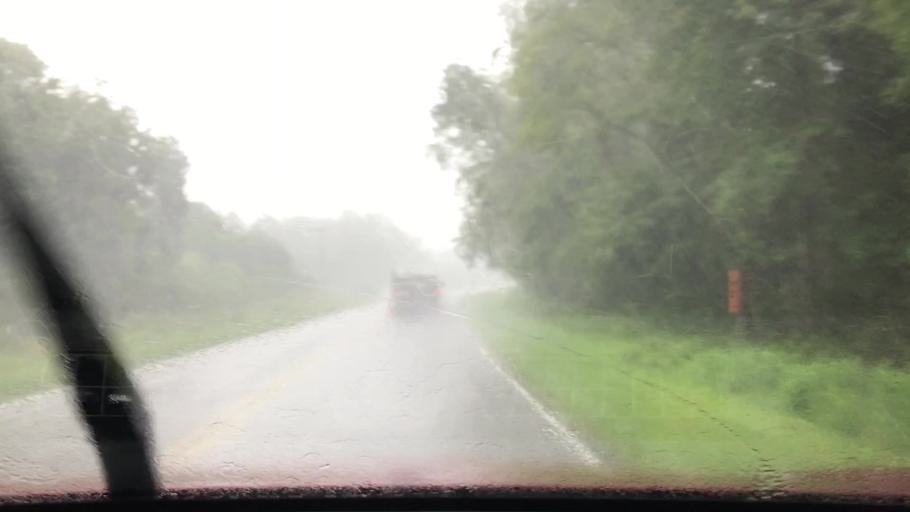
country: US
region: South Carolina
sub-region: Horry County
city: Red Hill
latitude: 33.9039
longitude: -78.9101
